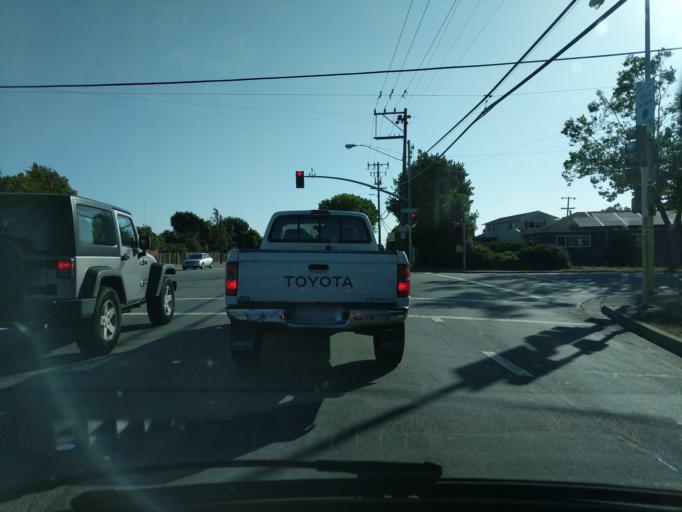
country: US
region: California
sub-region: Alameda County
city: San Lorenzo
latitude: 37.6815
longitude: -122.1501
